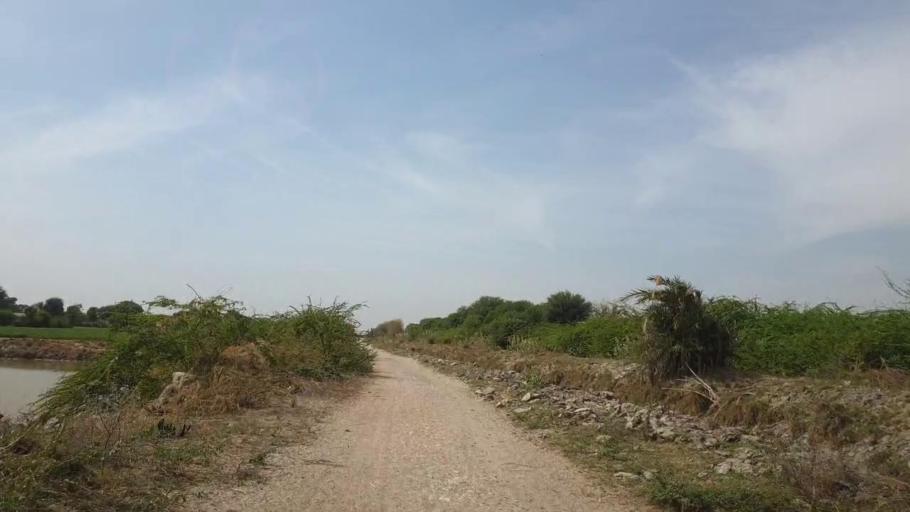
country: PK
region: Sindh
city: Kunri
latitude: 25.1945
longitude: 69.5674
